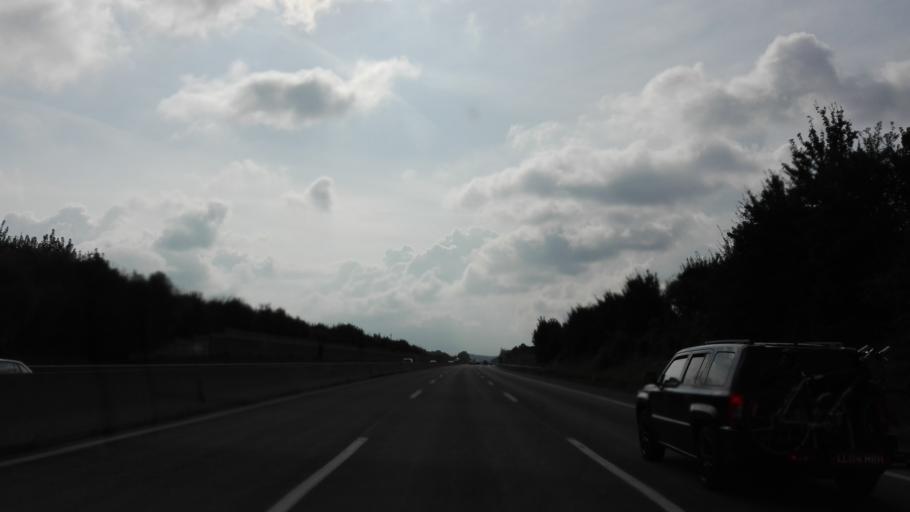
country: AT
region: Lower Austria
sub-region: Politischer Bezirk Melk
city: Blindenmarkt
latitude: 48.1345
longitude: 14.9866
